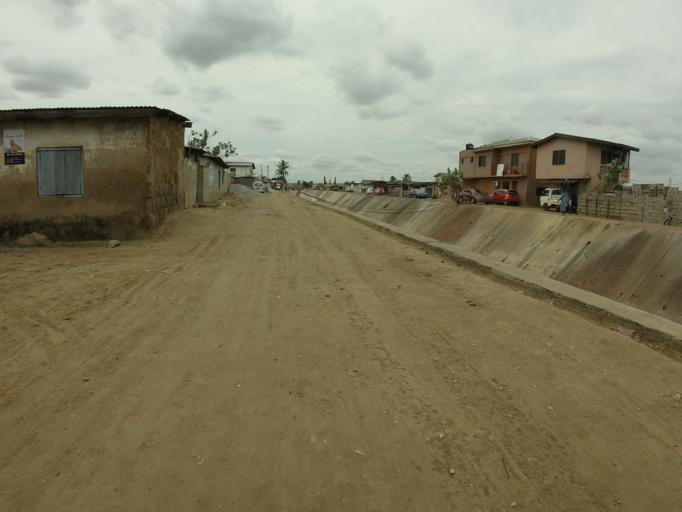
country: GH
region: Greater Accra
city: Accra
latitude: 5.5942
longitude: -0.2134
